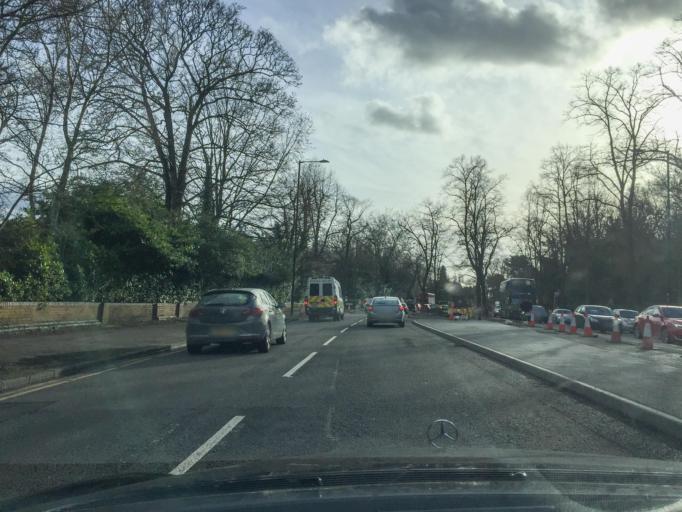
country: GB
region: England
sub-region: City and Borough of Birmingham
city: Birmingham
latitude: 52.4539
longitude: -1.9119
